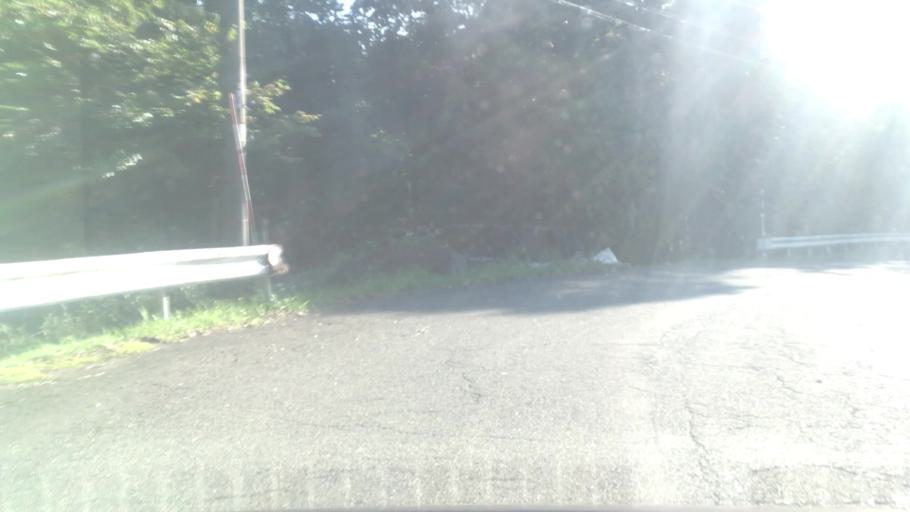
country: JP
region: Hyogo
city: Toyooka
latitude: 35.6096
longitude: 134.8321
